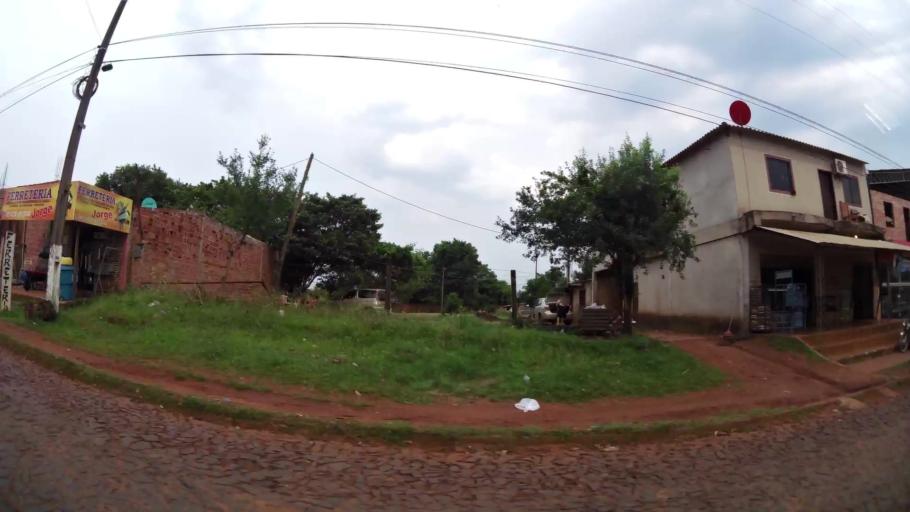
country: PY
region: Alto Parana
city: Presidente Franco
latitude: -25.5338
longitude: -54.6491
